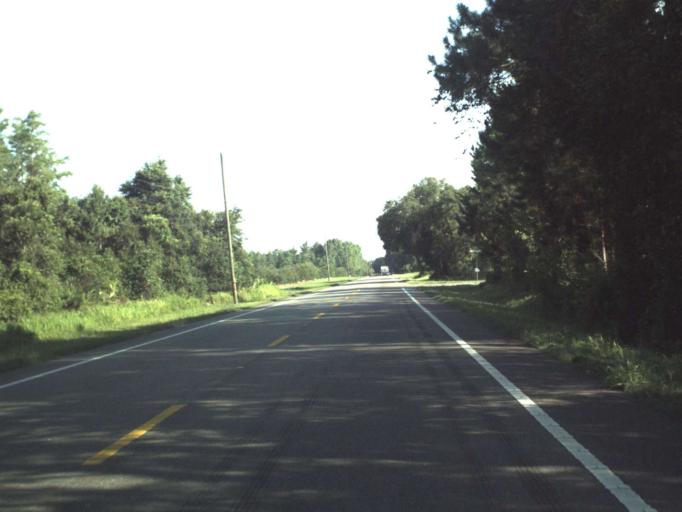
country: US
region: Florida
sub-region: Lake County
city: Groveland
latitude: 28.4210
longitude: -81.8317
